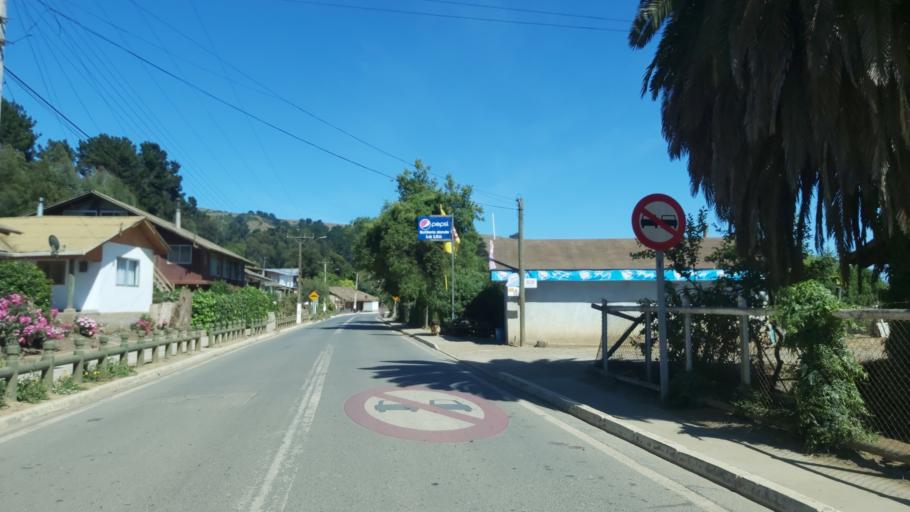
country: CL
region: Maule
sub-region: Provincia de Talca
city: Constitucion
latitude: -34.7658
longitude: -72.0760
